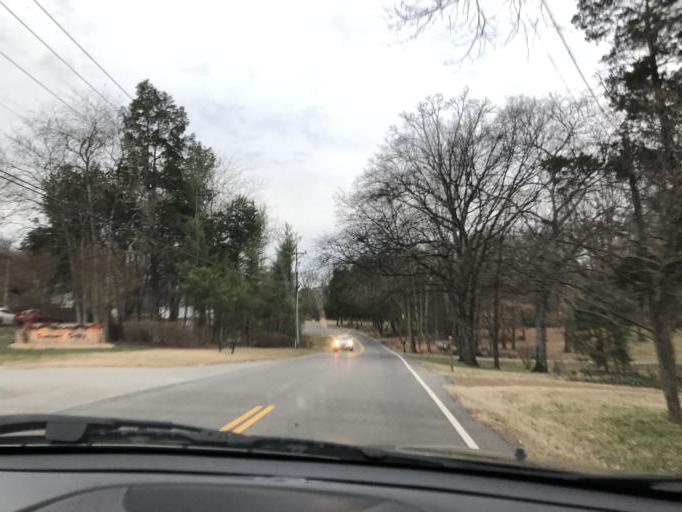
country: US
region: Tennessee
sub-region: Wilson County
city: Green Hill
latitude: 36.1931
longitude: -86.5921
